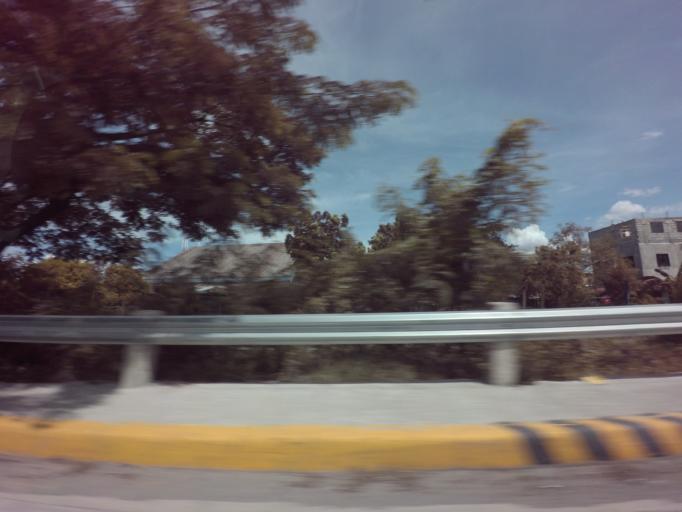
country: PH
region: Calabarzon
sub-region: Province of Rizal
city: Taguig
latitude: 14.5116
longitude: 121.0717
